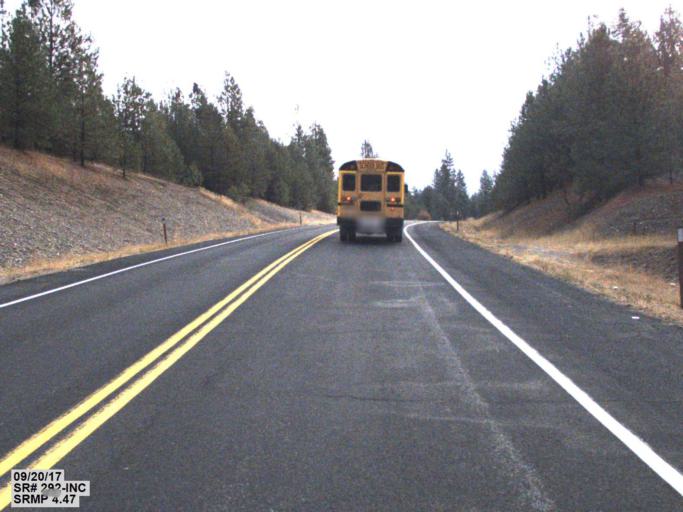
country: US
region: Washington
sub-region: Spokane County
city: Deer Park
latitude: 48.0652
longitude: -117.6497
